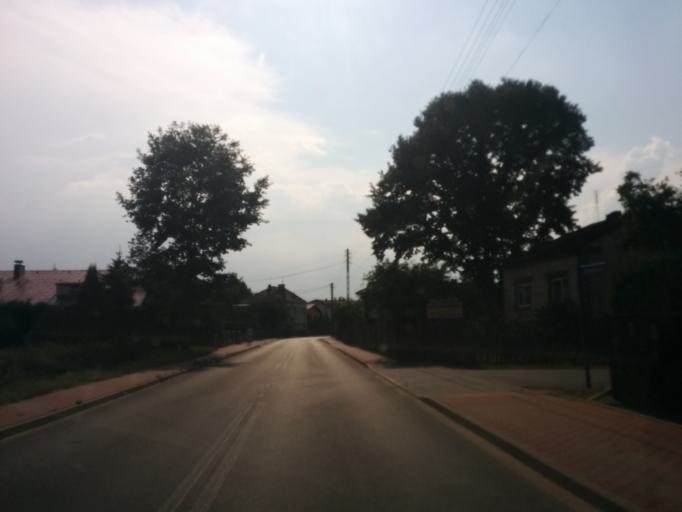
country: PL
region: Silesian Voivodeship
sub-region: Powiat myszkowski
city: Poraj
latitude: 50.6798
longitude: 19.2210
